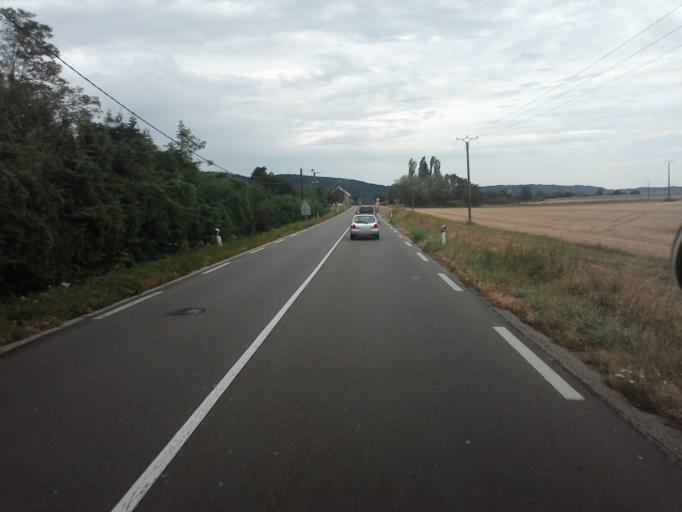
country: FR
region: Franche-Comte
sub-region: Departement du Jura
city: Poligny
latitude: 46.8721
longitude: 5.7163
